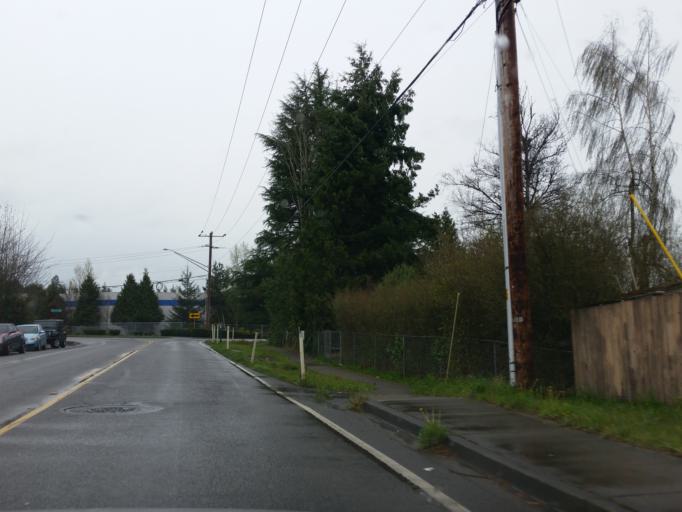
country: US
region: Washington
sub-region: Snohomish County
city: Martha Lake
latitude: 47.8762
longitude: -122.2474
